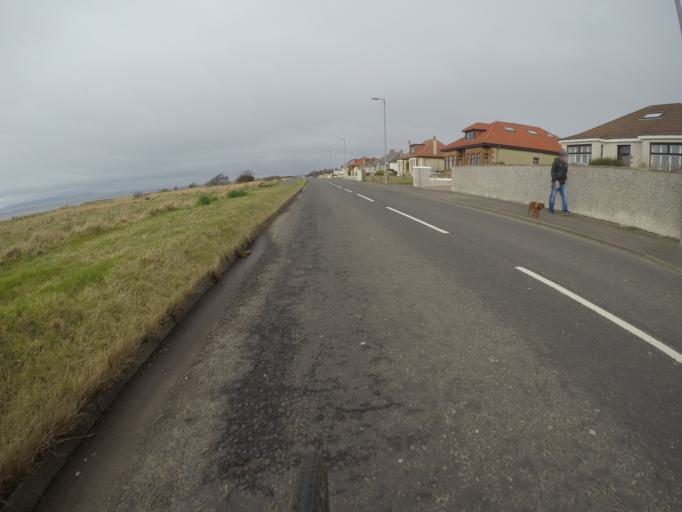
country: GB
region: Scotland
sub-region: North Ayrshire
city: Ardrossan
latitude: 55.6495
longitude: -4.8157
